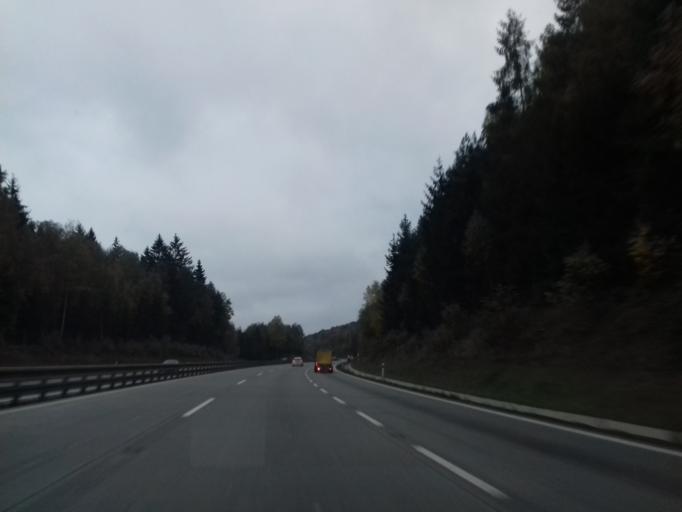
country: CZ
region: Central Bohemia
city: Divisov
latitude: 49.7668
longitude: 14.9492
